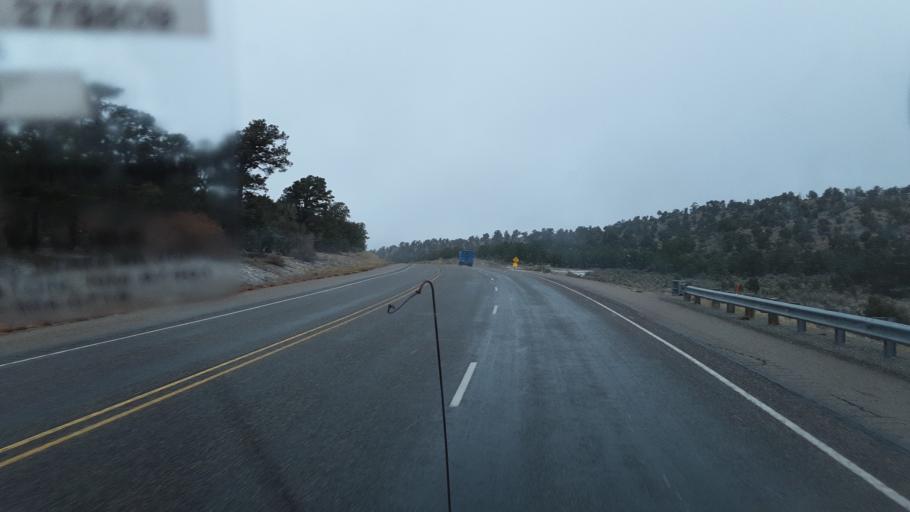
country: US
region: New Mexico
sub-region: Rio Arriba County
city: Tierra Amarilla
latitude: 36.4658
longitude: -106.4793
